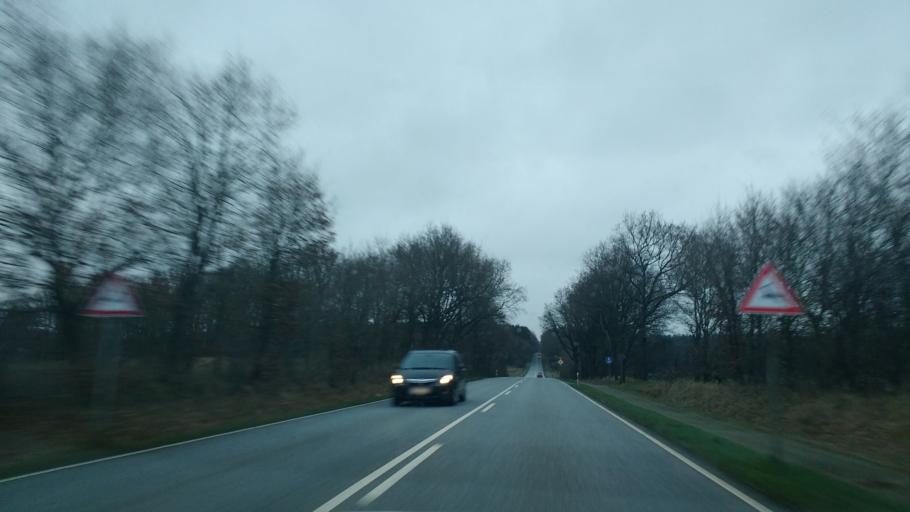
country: DE
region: Schleswig-Holstein
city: Silzen
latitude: 54.0370
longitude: 9.6083
